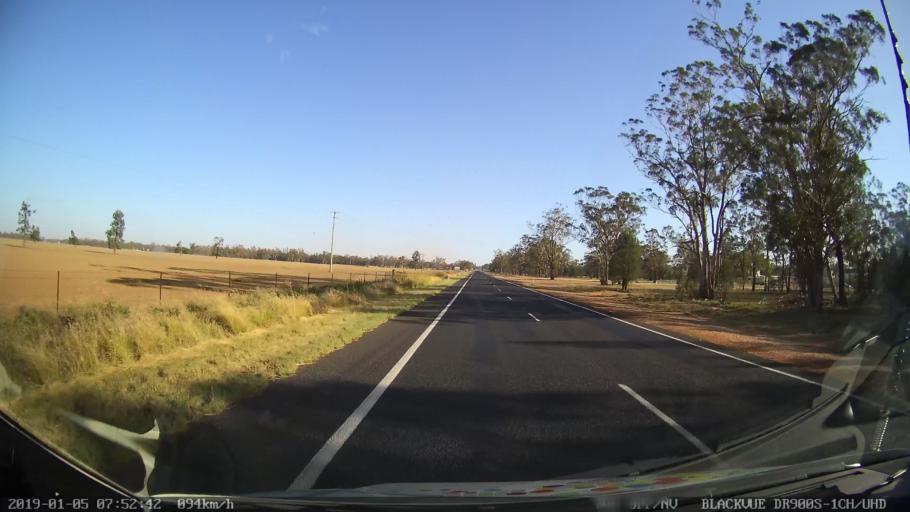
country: AU
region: New South Wales
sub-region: Gilgandra
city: Gilgandra
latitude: -31.7547
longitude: 148.6405
